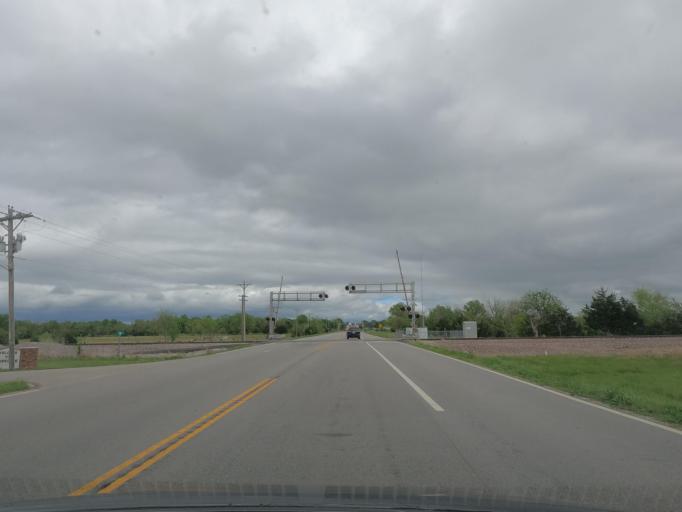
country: US
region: Kansas
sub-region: Crawford County
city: Pittsburg
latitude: 37.3393
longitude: -94.8211
